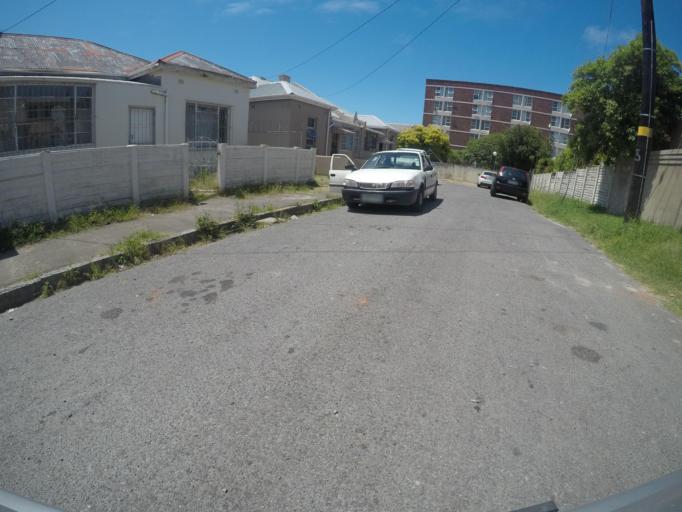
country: ZA
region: Eastern Cape
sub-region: Buffalo City Metropolitan Municipality
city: East London
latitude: -33.0010
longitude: 27.9098
